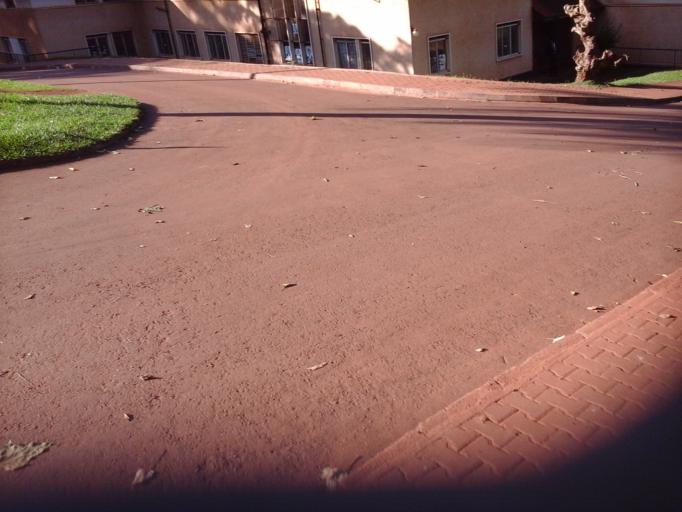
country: UG
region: Central Region
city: Kampala Central Division
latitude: 0.3381
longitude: 32.5677
